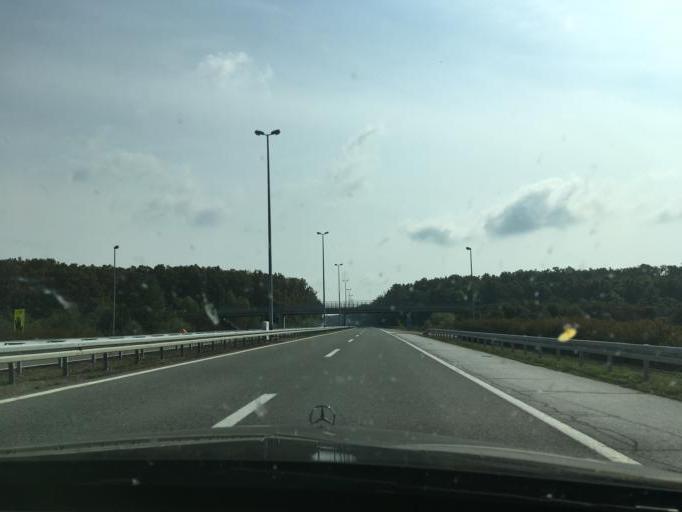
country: HR
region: Vukovarsko-Srijemska
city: Bosnjaci
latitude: 45.0571
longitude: 18.8127
